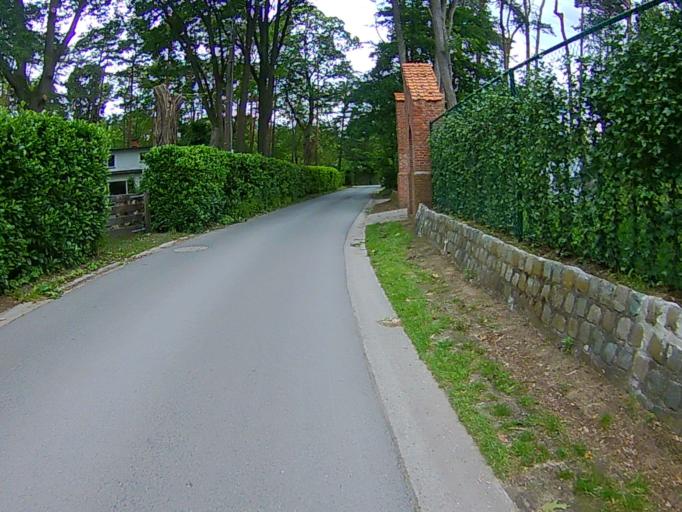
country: BE
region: Flanders
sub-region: Provincie Vlaams-Brabant
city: Keerbergen
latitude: 51.0086
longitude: 4.6179
